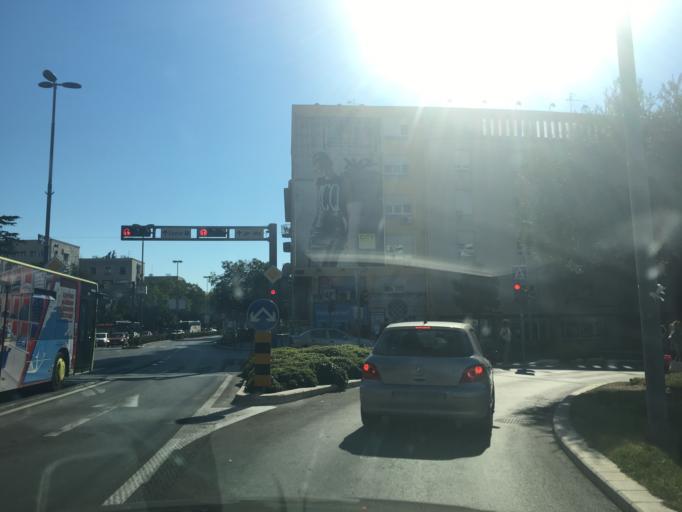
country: HR
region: Splitsko-Dalmatinska
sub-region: Grad Split
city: Split
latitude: 43.5150
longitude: 16.4436
